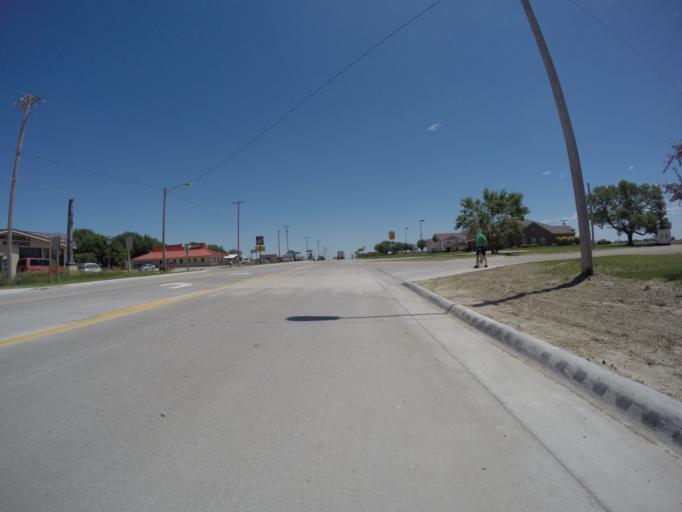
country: US
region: Kansas
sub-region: Republic County
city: Belleville
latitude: 39.8124
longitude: -97.6298
